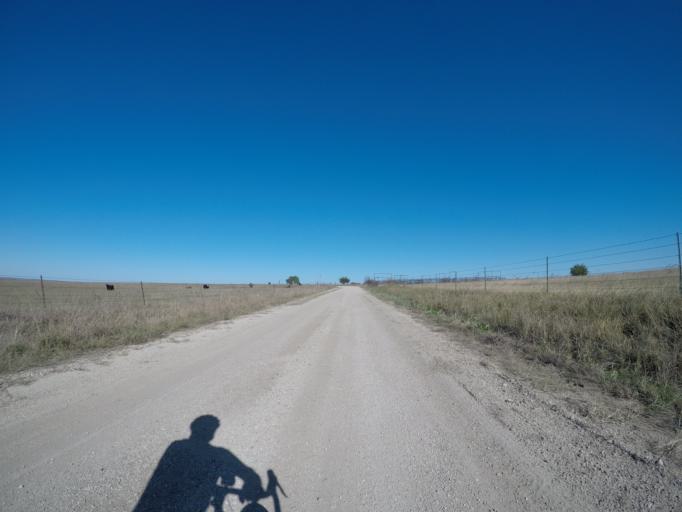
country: US
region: Kansas
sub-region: Wabaunsee County
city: Alma
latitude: 38.9188
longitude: -96.3882
